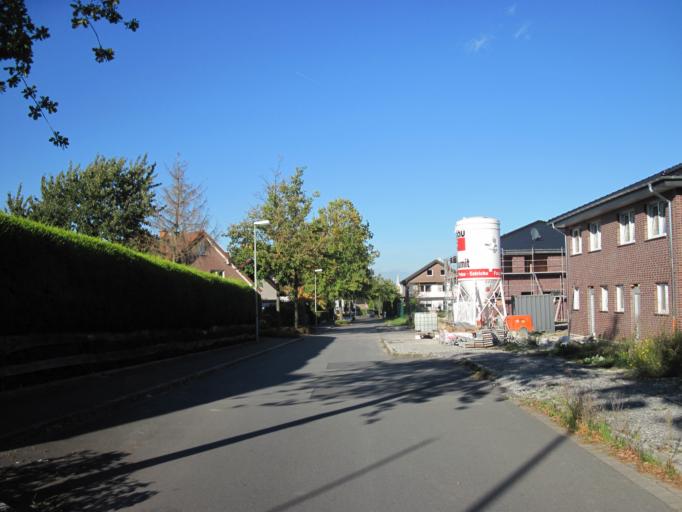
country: DE
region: North Rhine-Westphalia
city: Geseke
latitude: 51.6308
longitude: 8.5038
